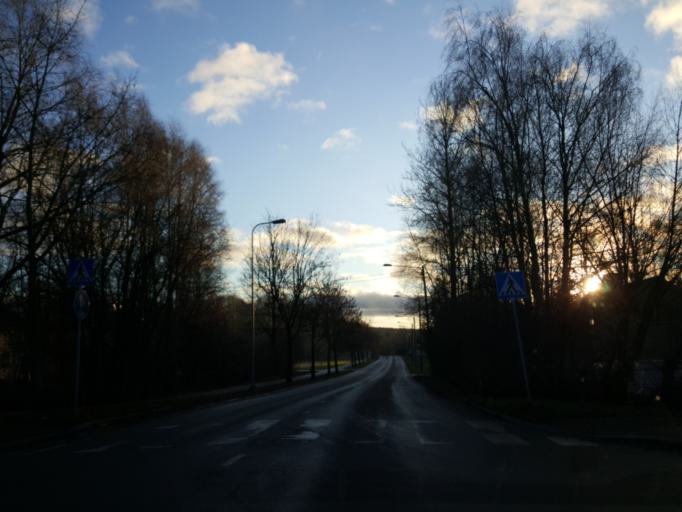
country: FI
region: Uusimaa
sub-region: Helsinki
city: Lohja
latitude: 60.2565
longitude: 24.0599
